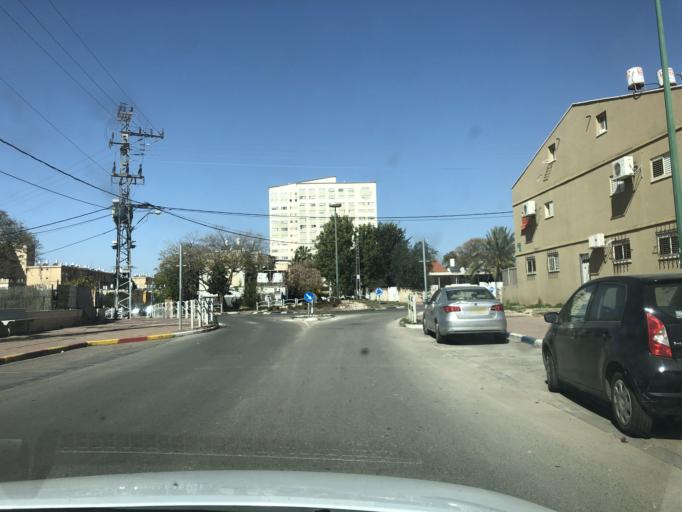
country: IL
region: Southern District
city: Beersheba
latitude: 31.2615
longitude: 34.7951
